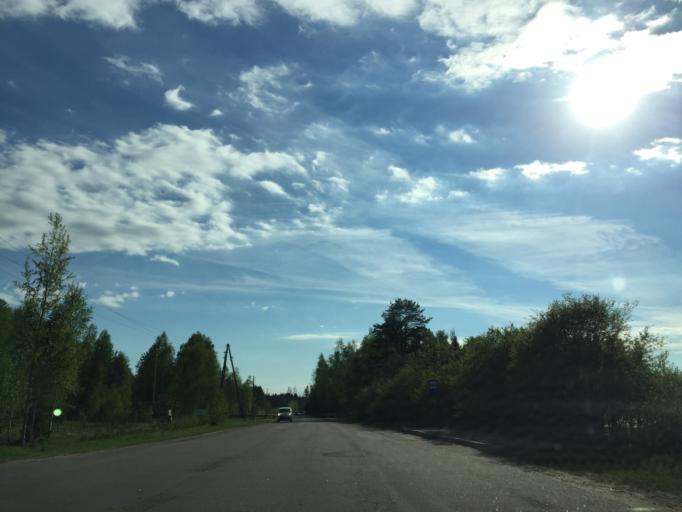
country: LV
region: Lecava
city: Iecava
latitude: 56.6939
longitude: 24.1113
